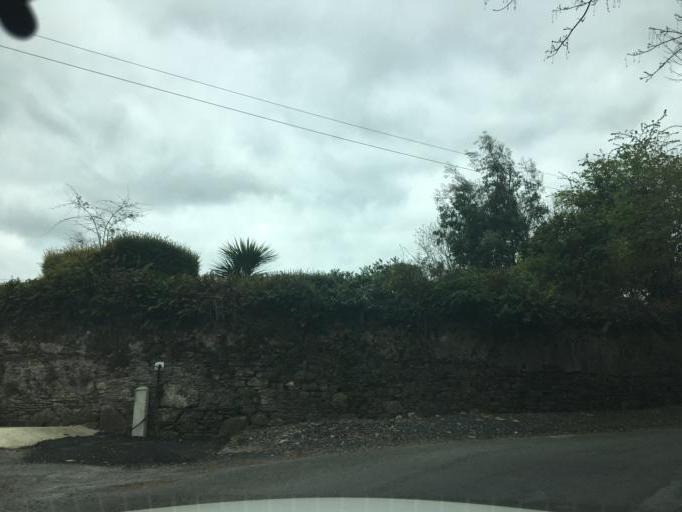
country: IE
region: Leinster
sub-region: Kilkenny
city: Thomastown
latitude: 52.4849
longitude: -7.0688
